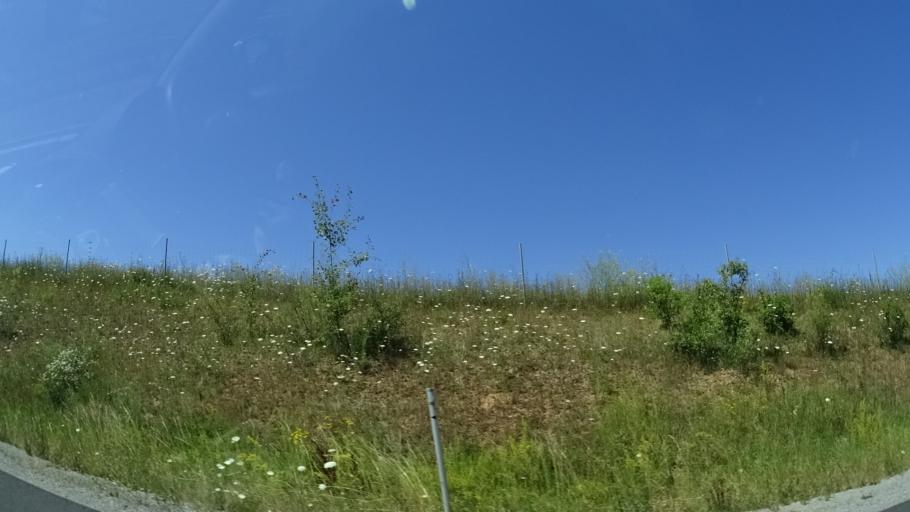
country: DE
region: Bavaria
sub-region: Regierungsbezirk Unterfranken
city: Geldersheim
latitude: 50.0444
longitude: 10.1398
